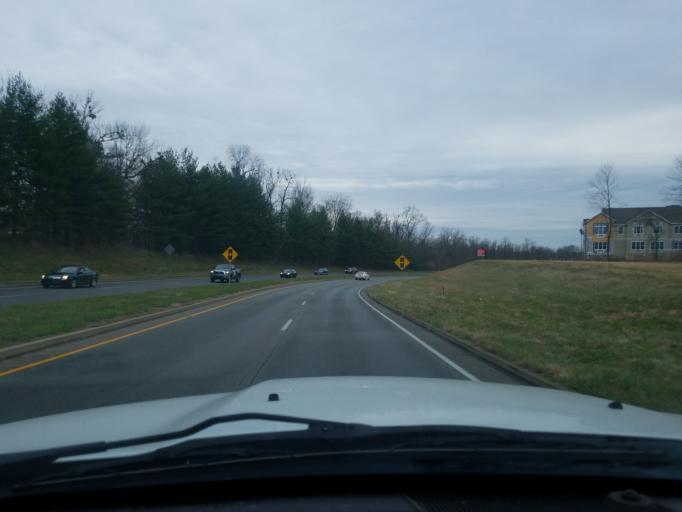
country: US
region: Kentucky
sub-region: Jefferson County
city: Anchorage
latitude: 38.2678
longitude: -85.5627
